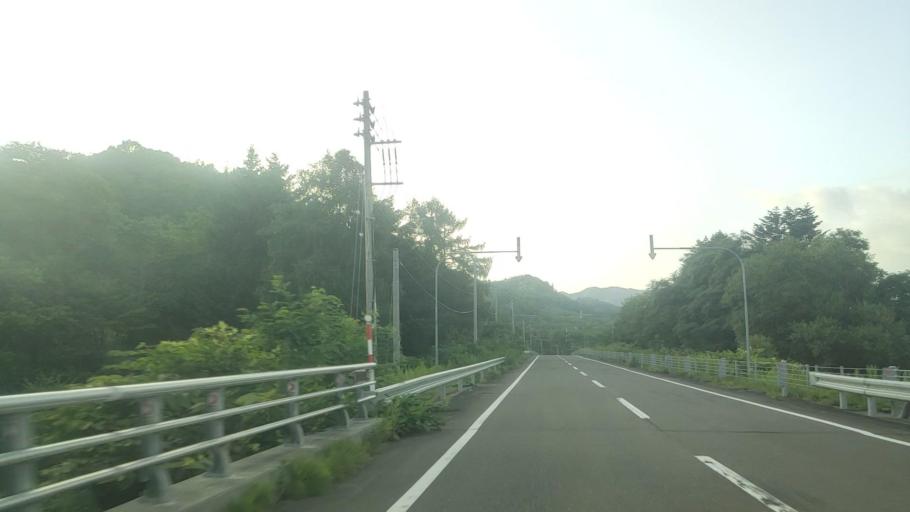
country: JP
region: Hokkaido
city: Bibai
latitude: 43.0792
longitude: 142.1010
